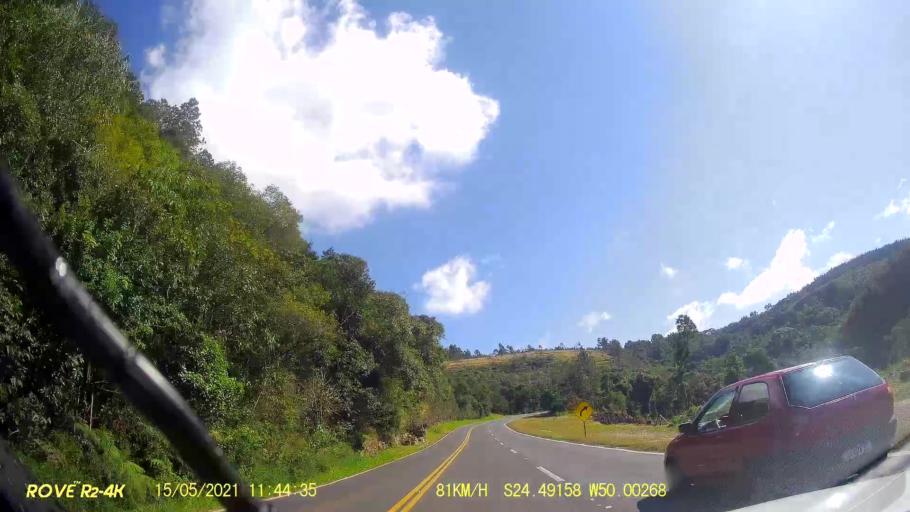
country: BR
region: Parana
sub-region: Pirai Do Sul
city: Pirai do Sul
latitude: -24.4916
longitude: -50.0025
